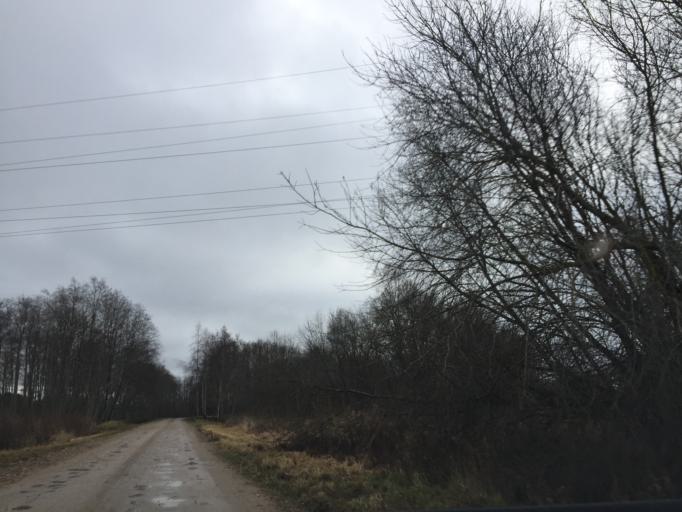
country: LV
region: Broceni
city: Broceni
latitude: 56.6744
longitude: 22.5581
